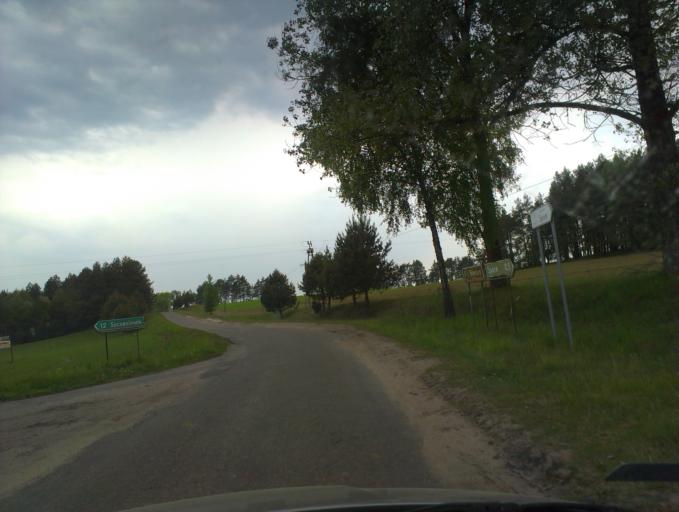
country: PL
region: West Pomeranian Voivodeship
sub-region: Powiat szczecinecki
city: Szczecinek
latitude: 53.8014
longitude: 16.6788
